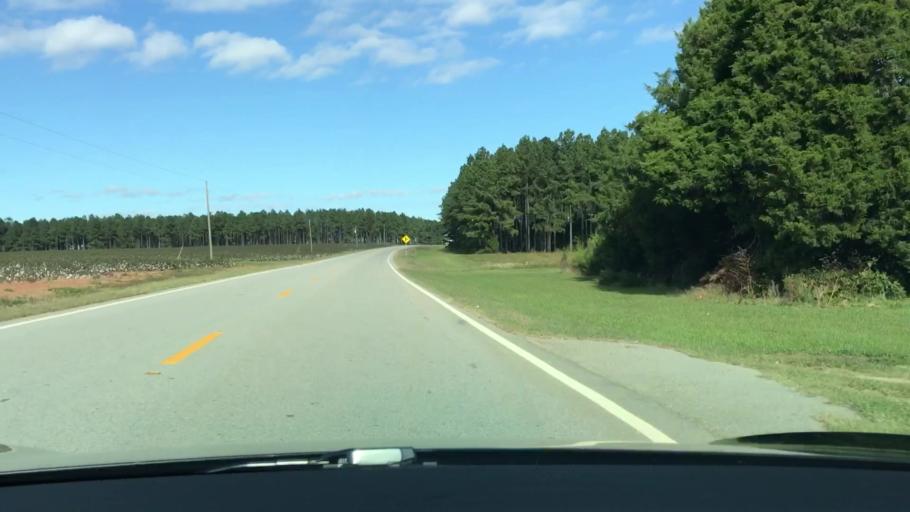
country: US
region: Georgia
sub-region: Glascock County
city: Gibson
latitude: 33.2763
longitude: -82.5016
